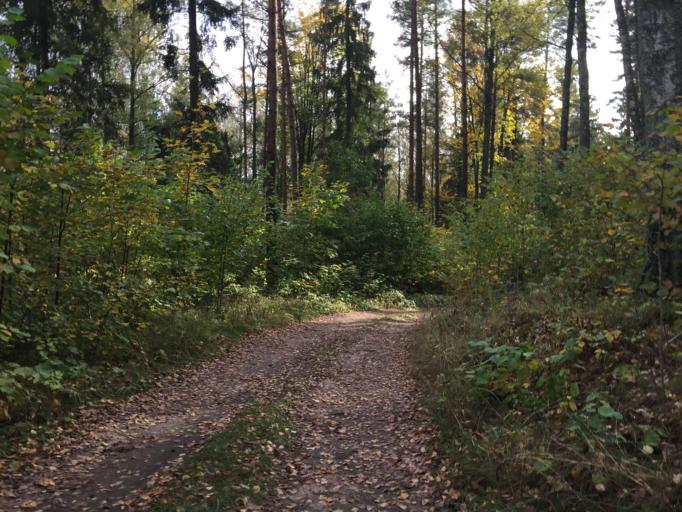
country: LV
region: Jaunpils
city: Jaunpils
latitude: 56.5982
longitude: 23.0146
